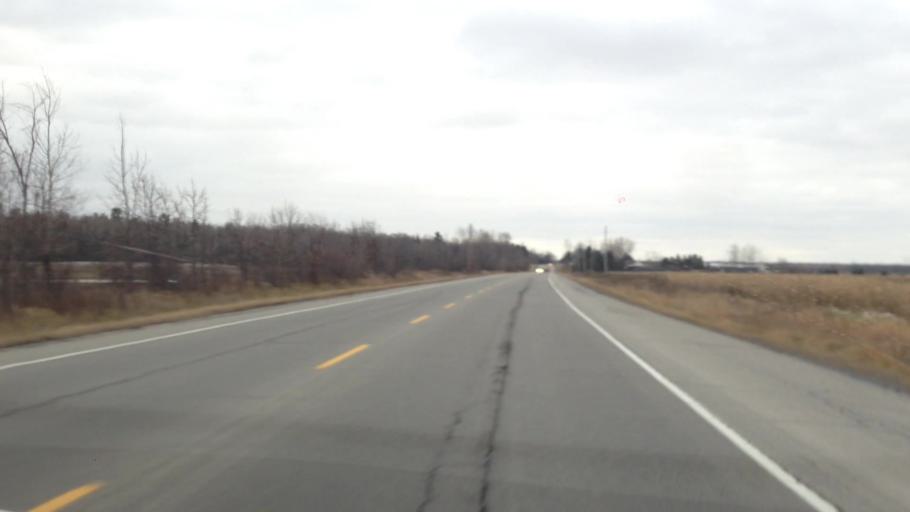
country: CA
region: Ontario
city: Clarence-Rockland
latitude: 45.3856
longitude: -75.3875
